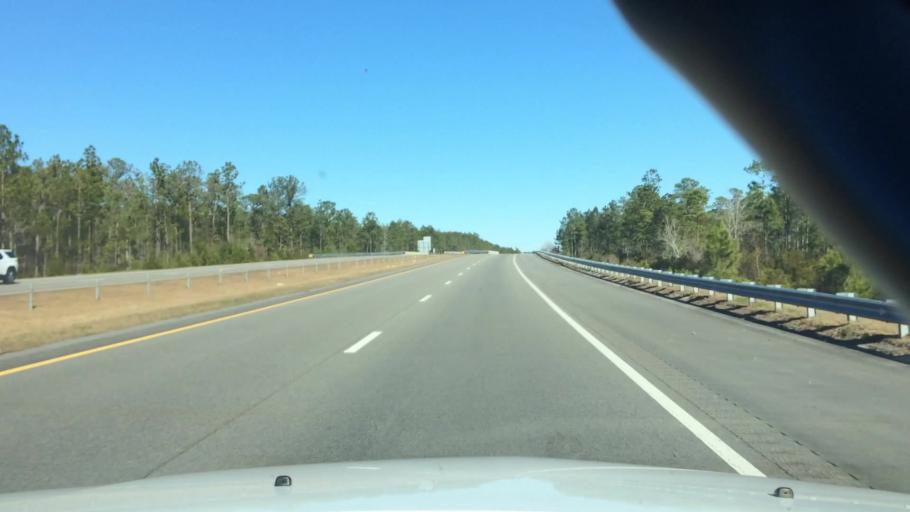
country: US
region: North Carolina
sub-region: Brunswick County
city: Leland
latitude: 34.2163
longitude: -78.0768
